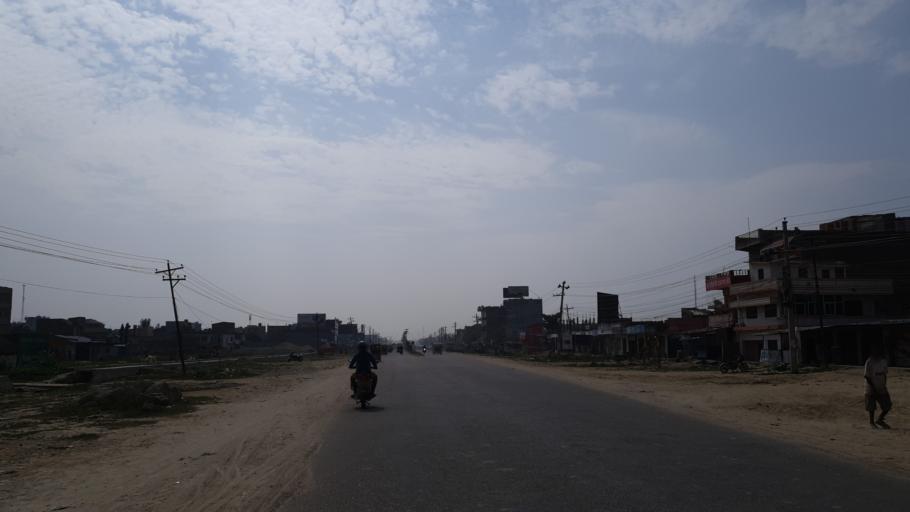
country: NP
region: Central Region
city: Janakpur
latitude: 26.7471
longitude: 85.9233
